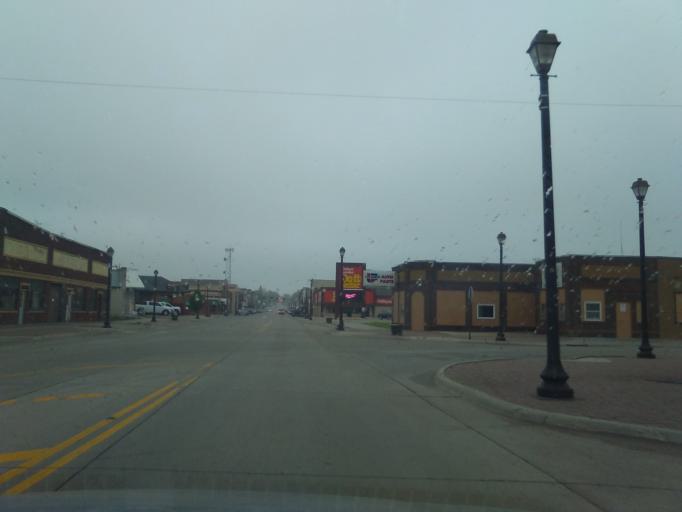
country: US
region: Nebraska
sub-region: Wayne County
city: Wayne
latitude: 42.2279
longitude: -97.0177
